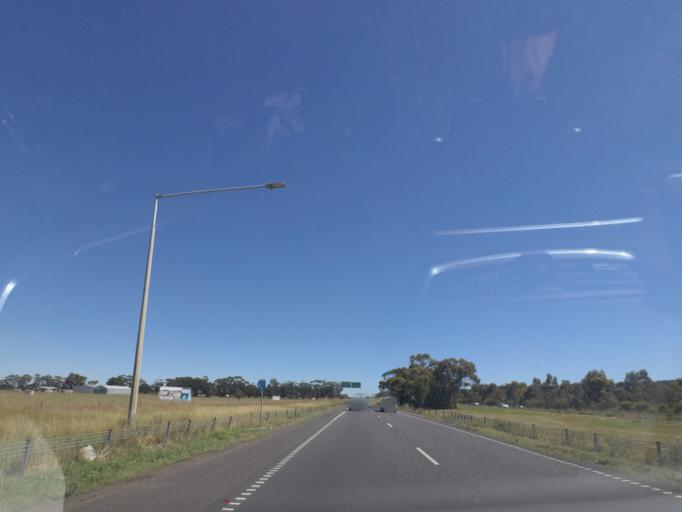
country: AU
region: Victoria
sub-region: Hume
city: Craigieburn
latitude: -37.5598
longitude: 144.9426
